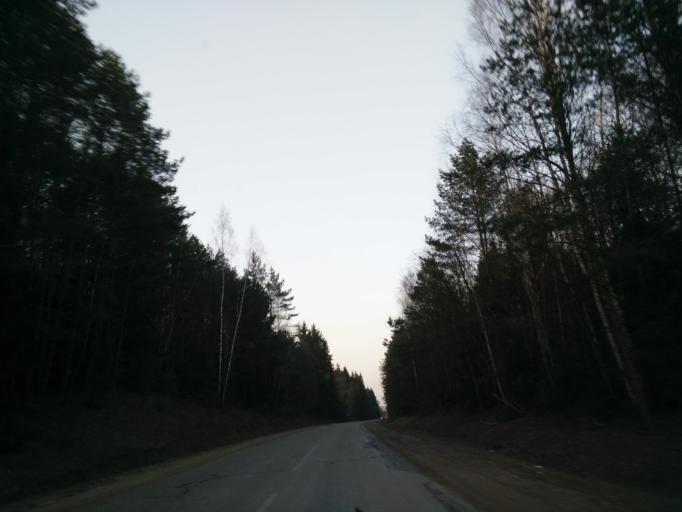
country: LT
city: Trakai
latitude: 54.7042
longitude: 24.9655
